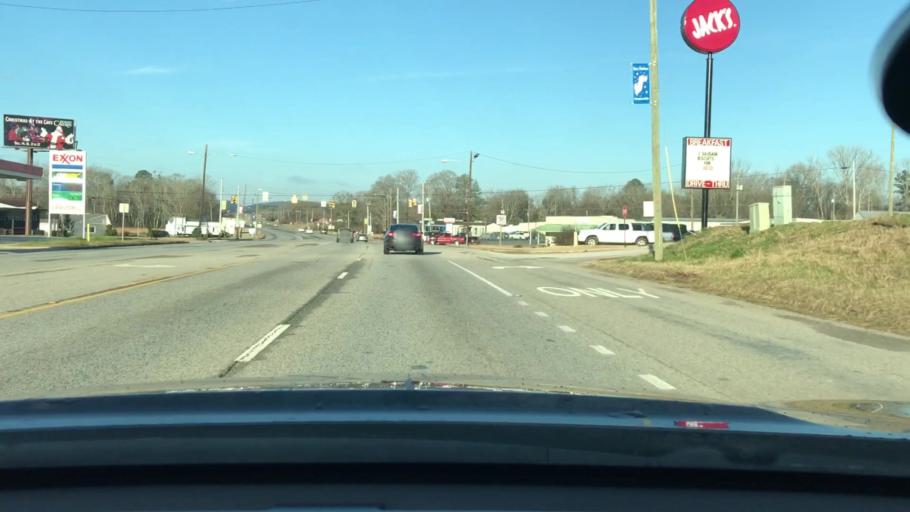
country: US
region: Alabama
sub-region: Shelby County
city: Harpersville
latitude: 33.3436
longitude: -86.4370
